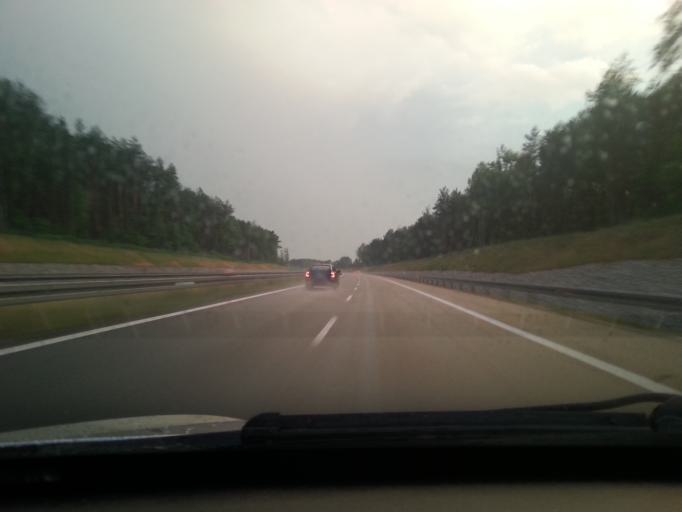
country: PL
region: Lodz Voivodeship
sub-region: Powiat pabianicki
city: Dobron
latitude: 51.6630
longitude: 19.2782
